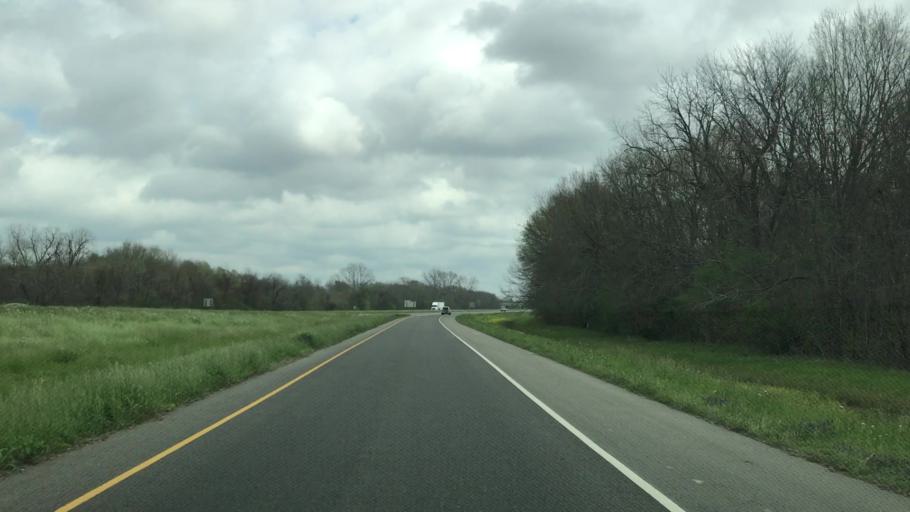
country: US
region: Louisiana
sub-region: Rapides Parish
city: Boyce
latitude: 31.3793
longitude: -92.6650
